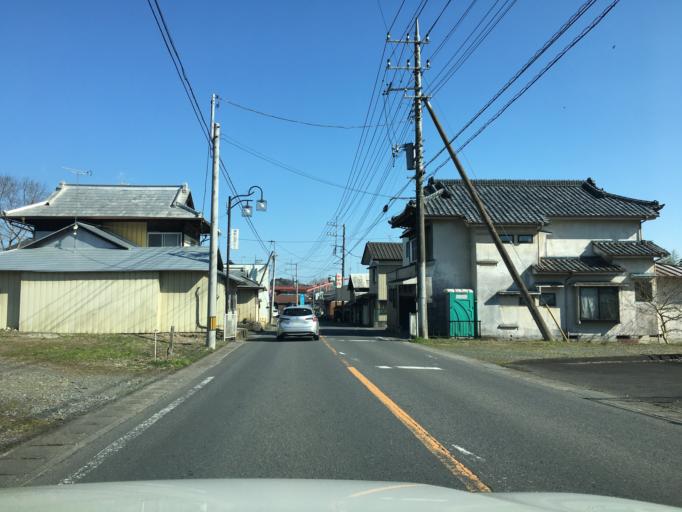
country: JP
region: Ibaraki
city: Omiya
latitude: 36.5492
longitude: 140.3292
